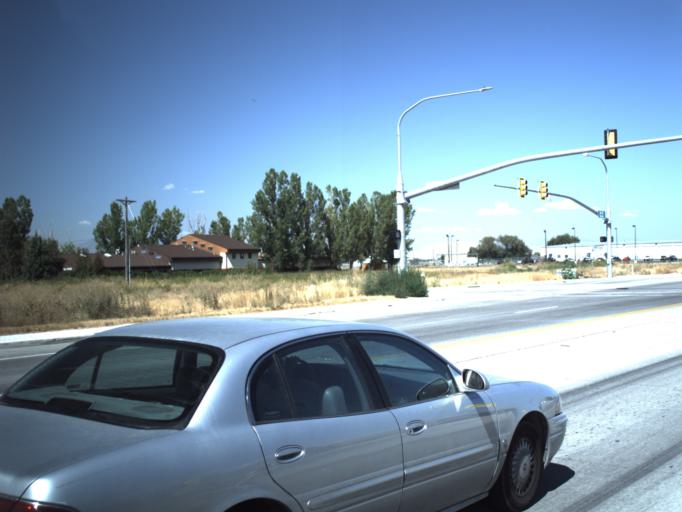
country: US
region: Utah
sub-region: Cache County
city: Logan
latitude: 41.7575
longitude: -111.8587
